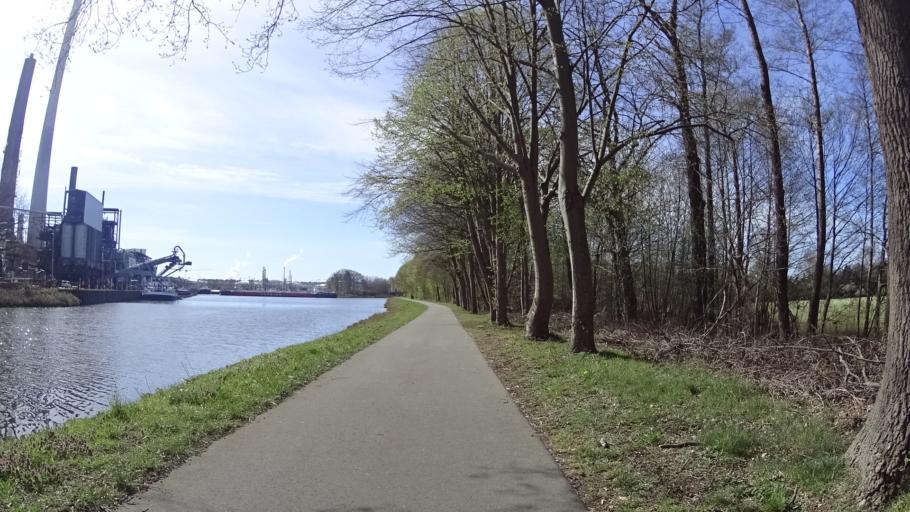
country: DE
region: Lower Saxony
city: Lingen
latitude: 52.5639
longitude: 7.3012
